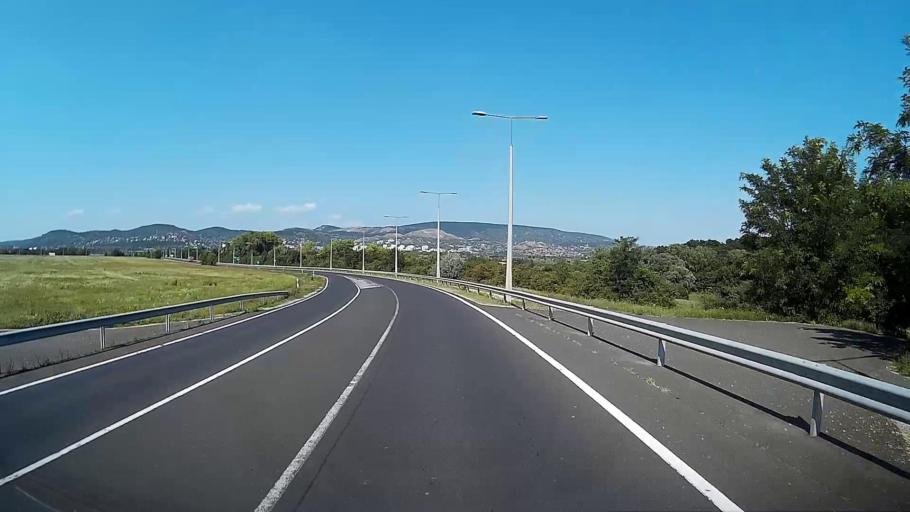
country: HU
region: Pest
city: Toeroekbalint
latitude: 47.4344
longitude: 18.9365
